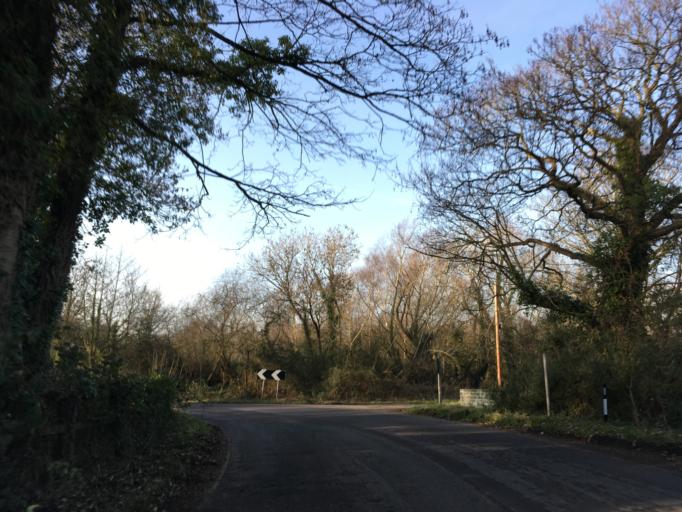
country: GB
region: Wales
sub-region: Newport
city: Nash
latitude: 51.5617
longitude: -2.9406
